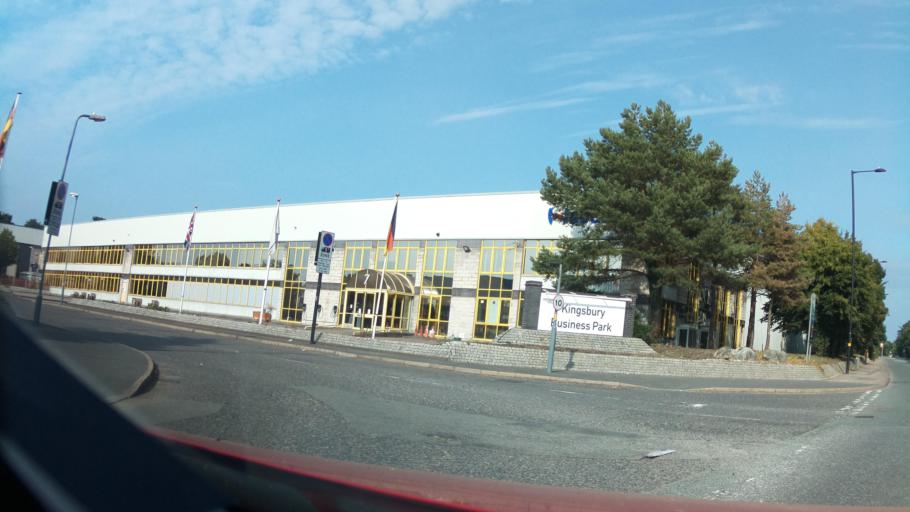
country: GB
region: England
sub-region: Warwickshire
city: Curdworth
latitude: 52.5293
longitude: -1.7616
